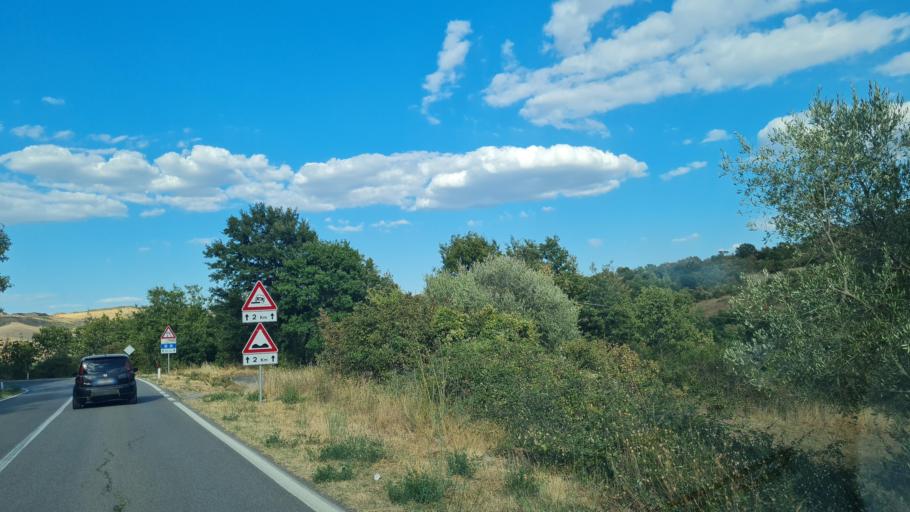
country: IT
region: Tuscany
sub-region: Provincia di Siena
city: Abbadia San Salvatore
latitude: 42.9318
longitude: 11.7007
